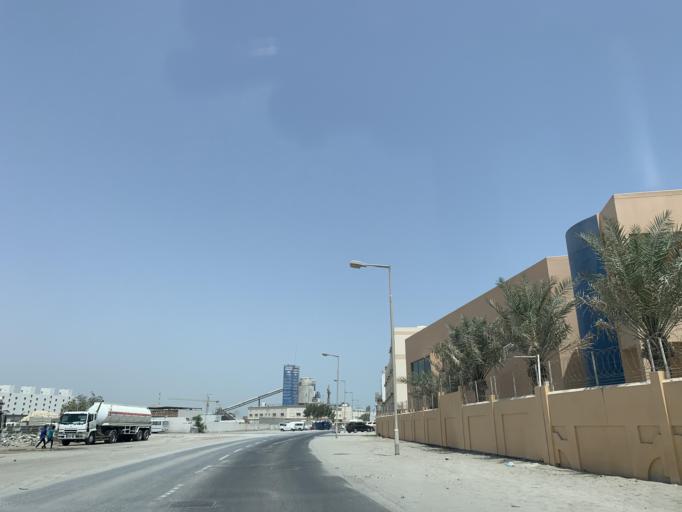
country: BH
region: Northern
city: Sitrah
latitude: 26.1452
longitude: 50.6002
